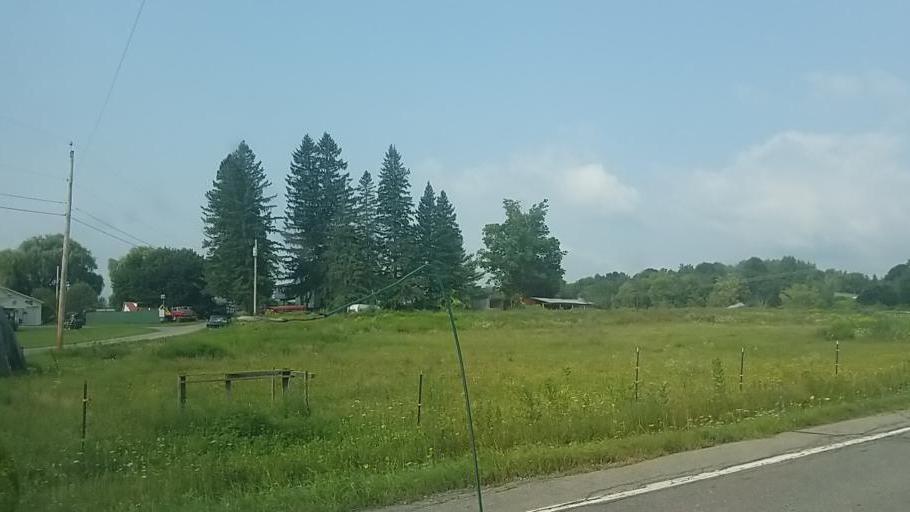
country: US
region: New York
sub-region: Fulton County
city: Johnstown
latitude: 43.0156
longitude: -74.3854
